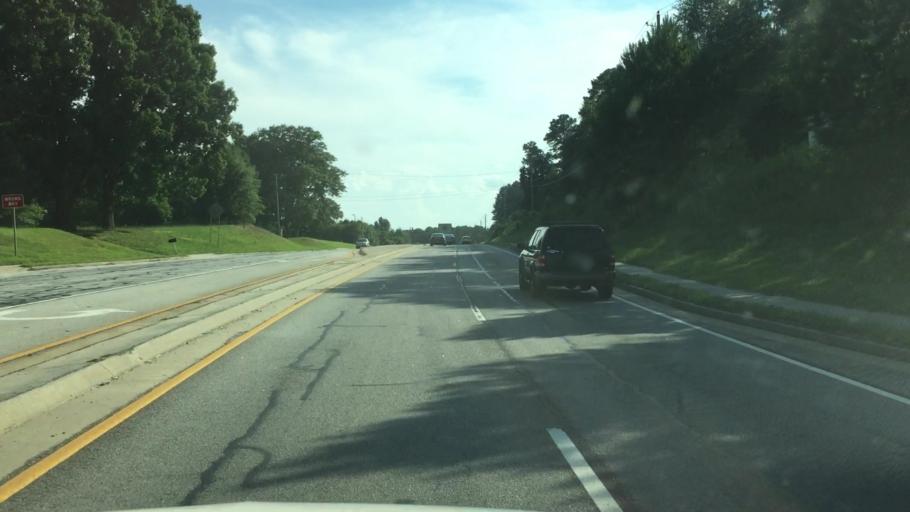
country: US
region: Georgia
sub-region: Gwinnett County
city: Snellville
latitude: 33.8483
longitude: -84.0252
